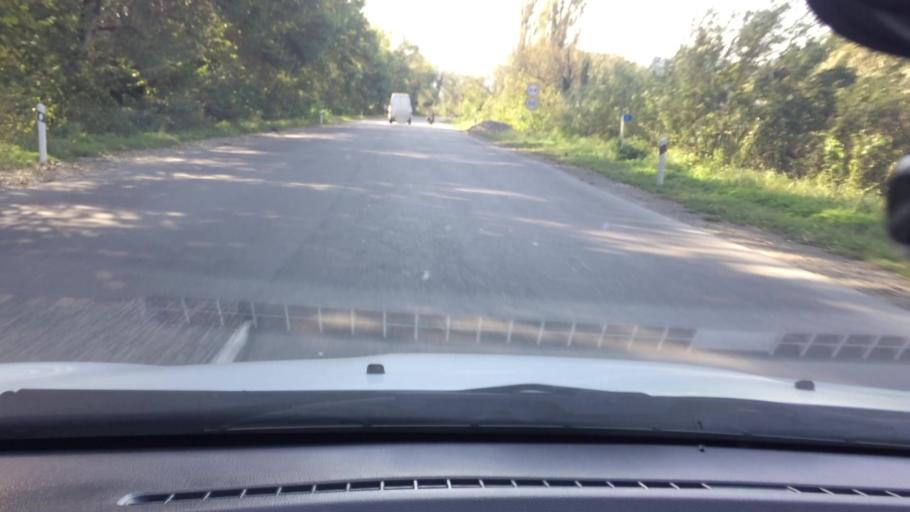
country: GE
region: Imereti
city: Samtredia
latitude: 42.1285
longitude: 42.3352
